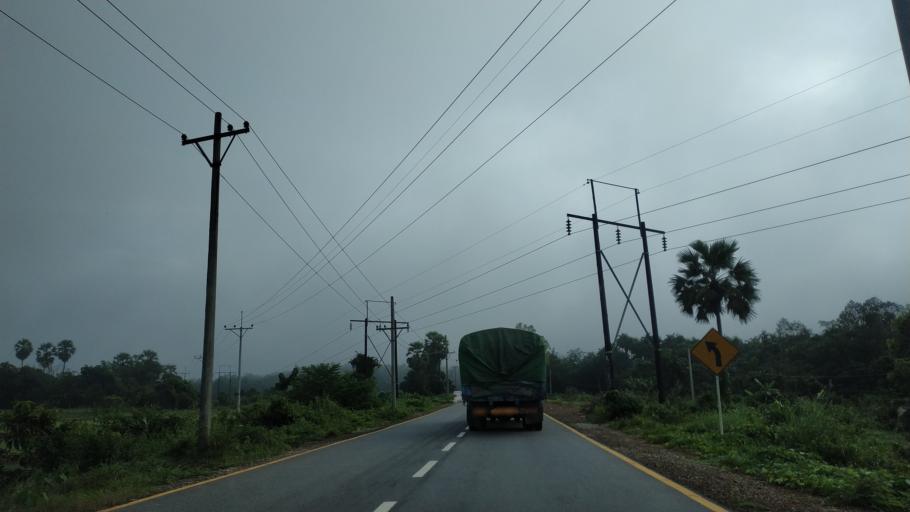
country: MM
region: Tanintharyi
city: Dawei
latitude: 14.2032
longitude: 98.2056
